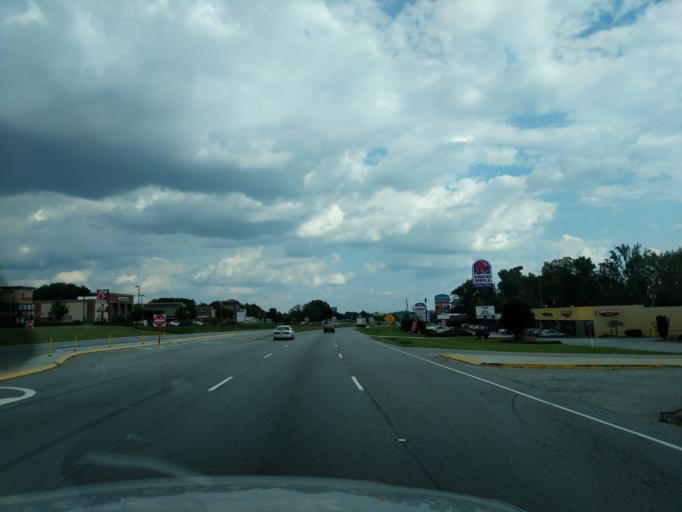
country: US
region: South Carolina
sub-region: Anderson County
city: Powdersville
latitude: 34.7877
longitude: -82.4806
